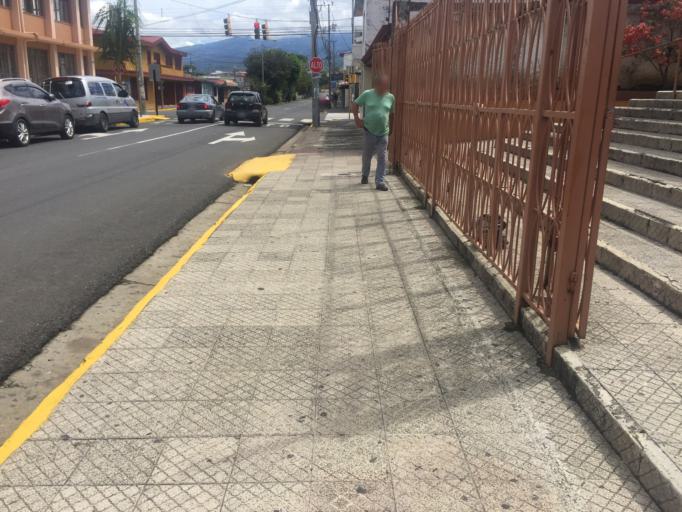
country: CR
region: Heredia
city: Heredia
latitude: 10.0029
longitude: -84.1192
